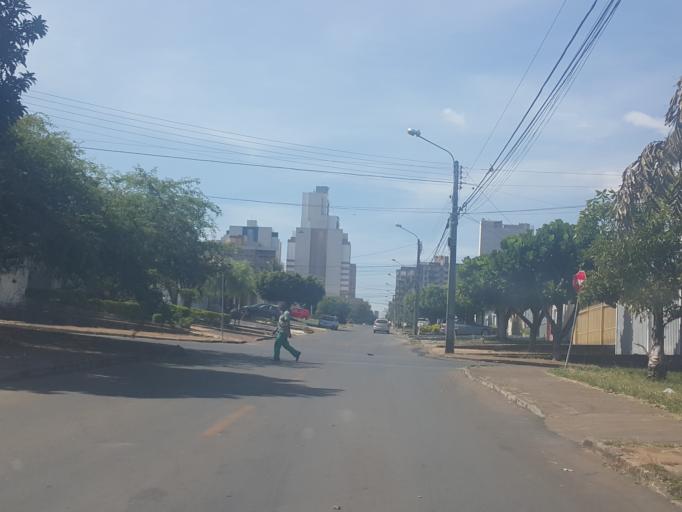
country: BR
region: Federal District
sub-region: Brasilia
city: Brasilia
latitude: -15.8256
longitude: -48.0654
